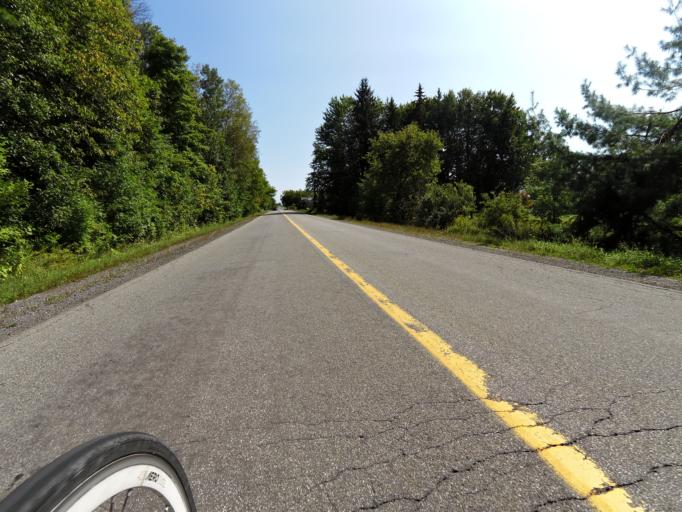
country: CA
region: Ontario
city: Arnprior
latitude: 45.4965
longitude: -76.1452
